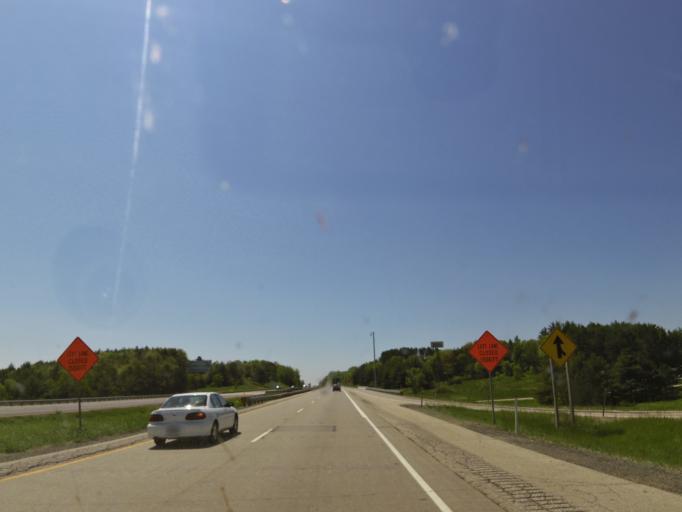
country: US
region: Wisconsin
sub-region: Monroe County
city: Tomah
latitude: 44.1258
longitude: -90.5337
